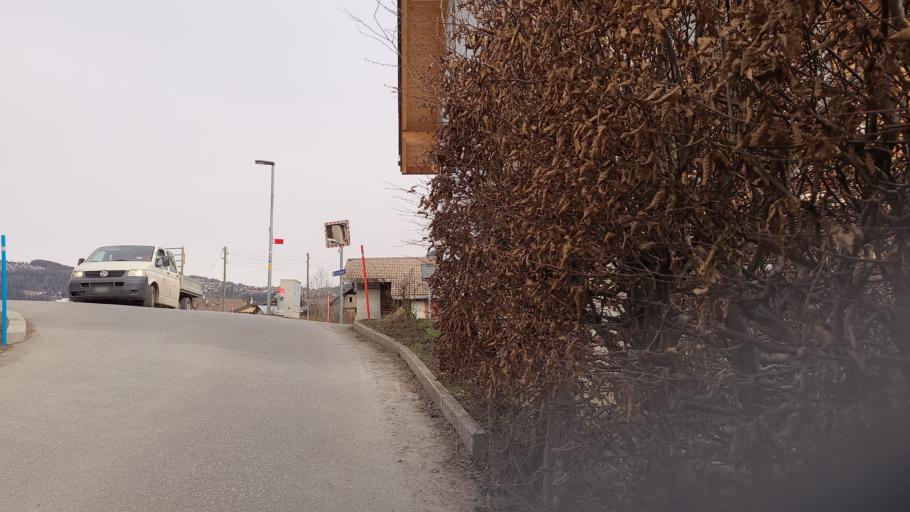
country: CH
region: Valais
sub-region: Herens District
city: Ayent
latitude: 46.2740
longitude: 7.4108
